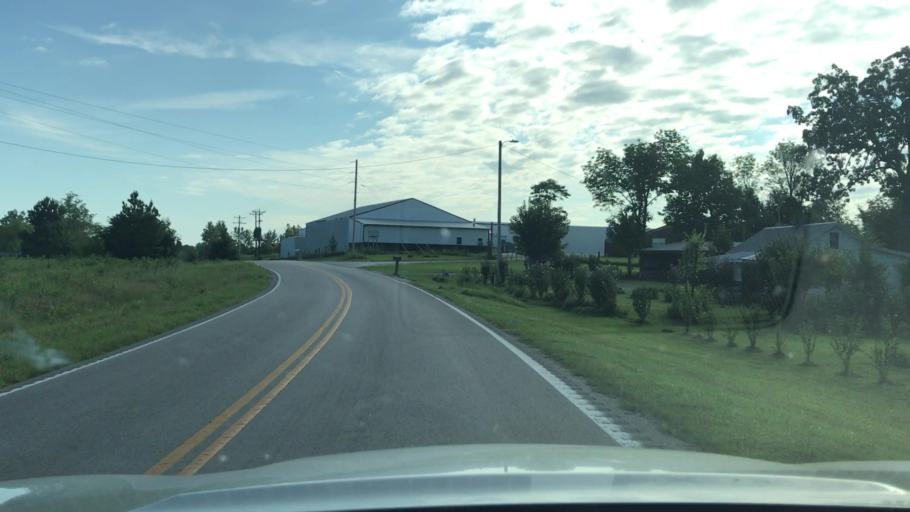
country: US
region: Kentucky
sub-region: Todd County
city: Elkton
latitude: 36.9338
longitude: -87.1572
